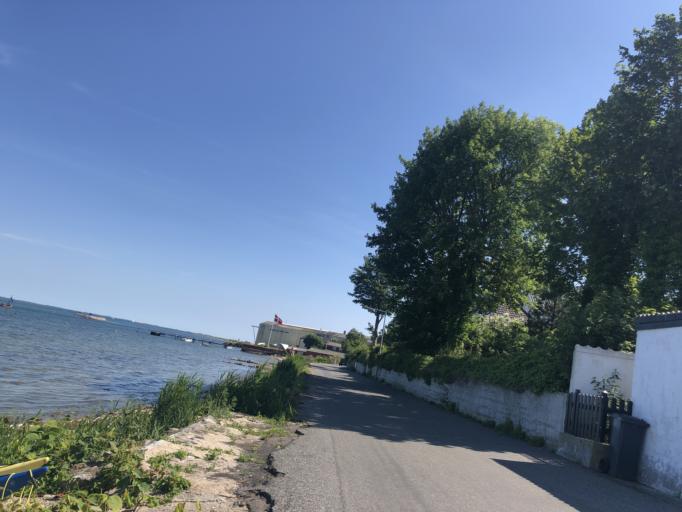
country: DK
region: South Denmark
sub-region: AEro Kommune
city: Marstal
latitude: 54.8599
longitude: 10.5185
